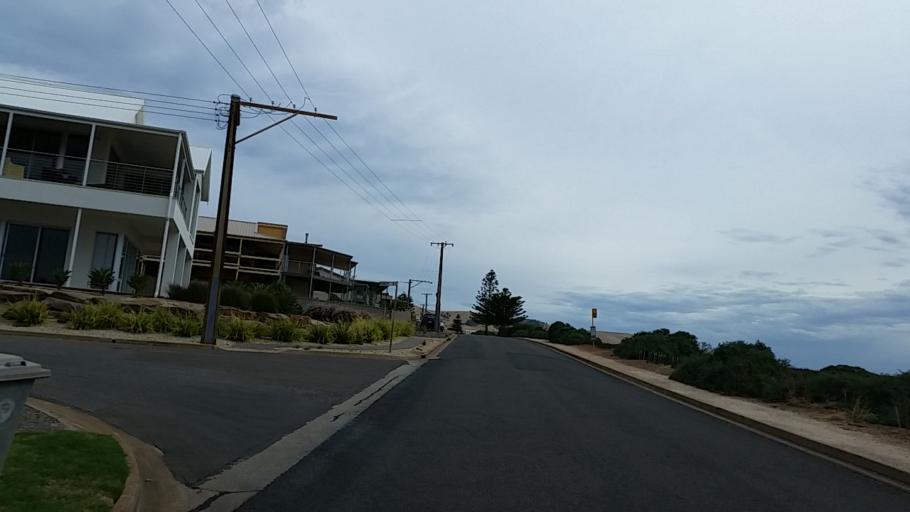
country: AU
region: South Australia
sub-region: Onkaparinga
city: Port Willunga
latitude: -35.3338
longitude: 138.4485
